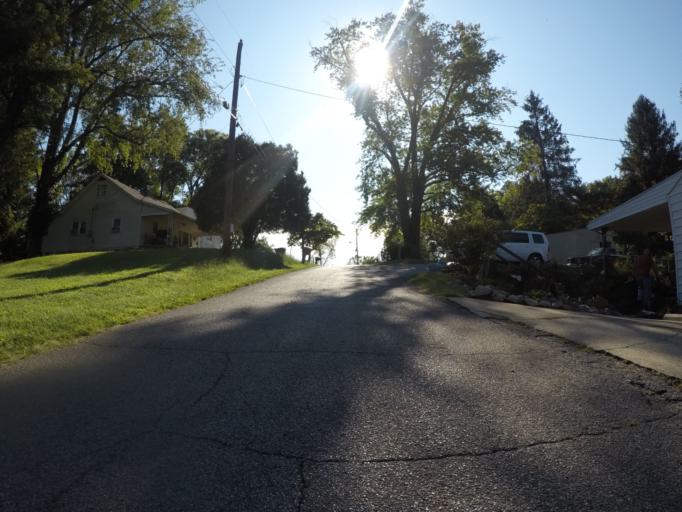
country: US
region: Kentucky
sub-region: Boyd County
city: Ashland
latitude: 38.4539
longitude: -82.6304
